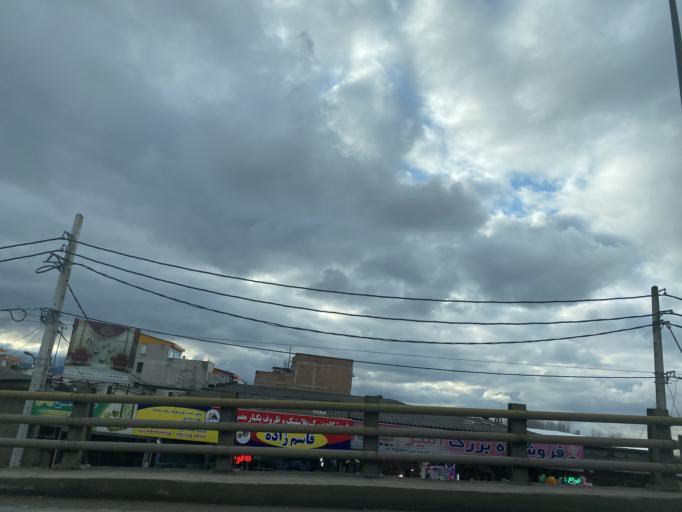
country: IR
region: Mazandaran
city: Amol
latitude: 36.4322
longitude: 52.3482
